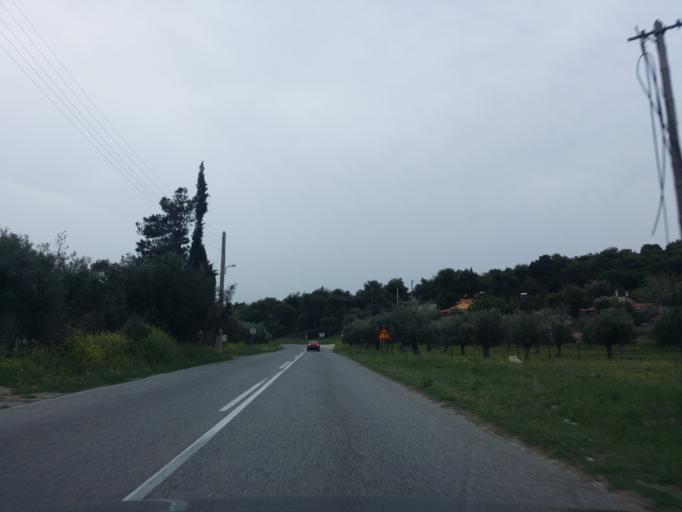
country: GR
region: Attica
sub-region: Nomarchia Dytikis Attikis
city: Mandra
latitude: 38.0865
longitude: 23.4834
